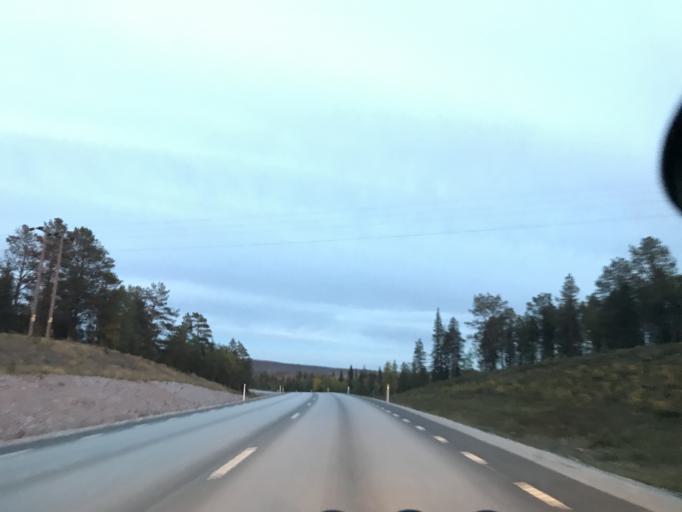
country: SE
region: Norrbotten
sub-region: Gallivare Kommun
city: Malmberget
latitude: 67.6488
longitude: 21.0228
